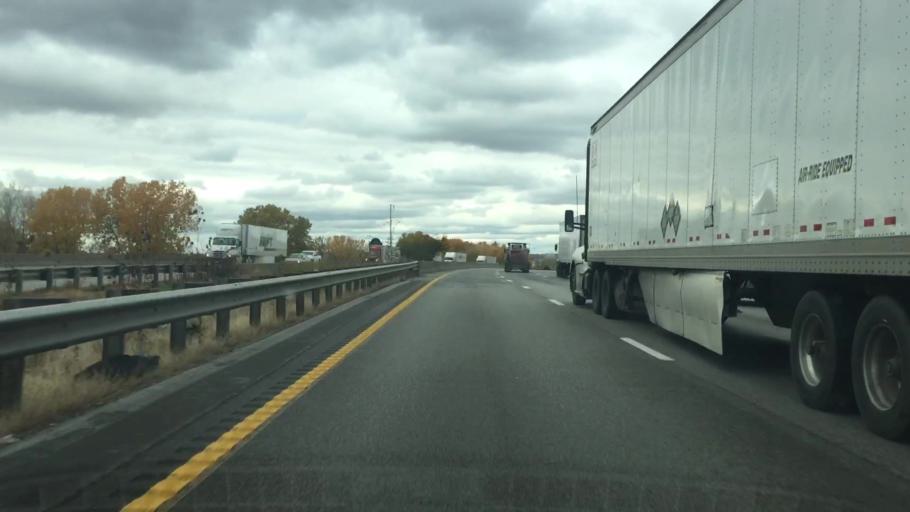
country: US
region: Missouri
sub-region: Jackson County
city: Sugar Creek
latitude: 39.1249
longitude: -94.4958
